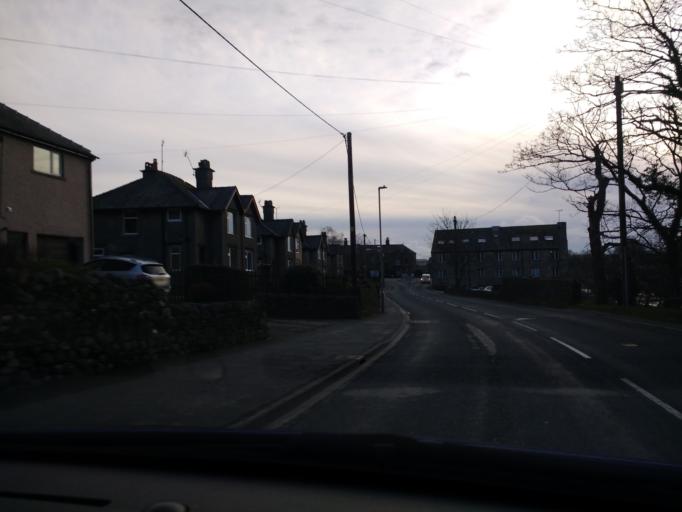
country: GB
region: England
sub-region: North Yorkshire
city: Settle
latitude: 54.0729
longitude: -2.2797
